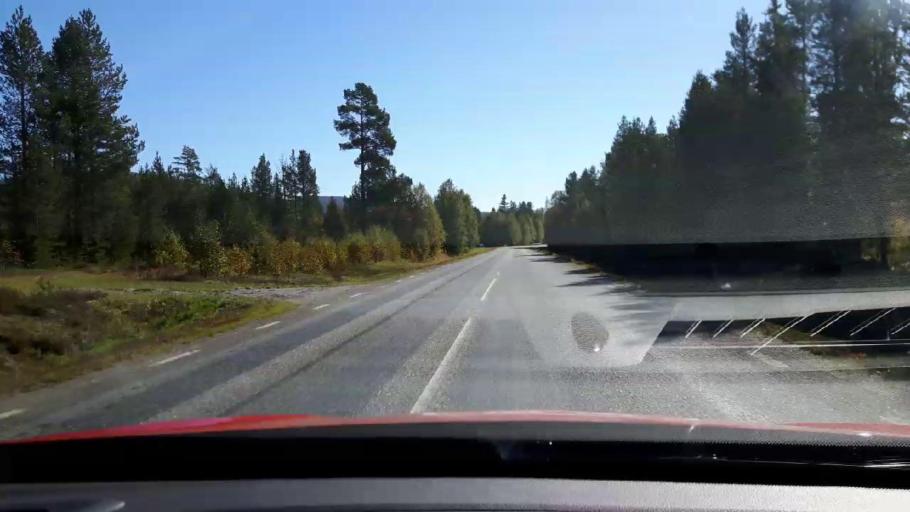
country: SE
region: Jaemtland
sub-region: Harjedalens Kommun
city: Sveg
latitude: 62.3535
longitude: 14.0241
